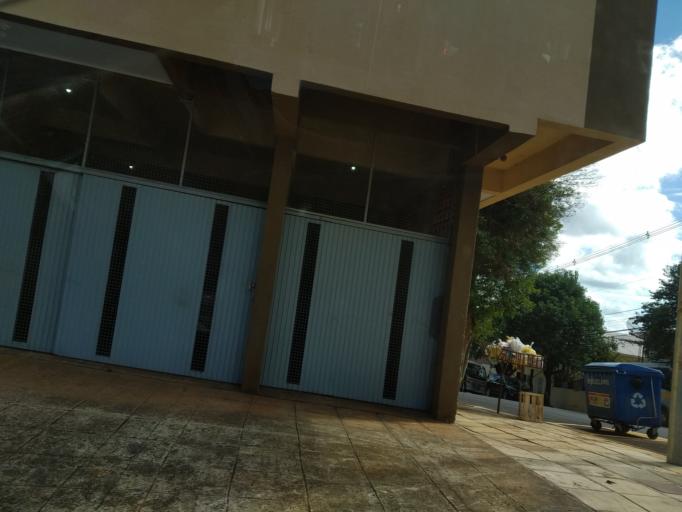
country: BR
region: Parana
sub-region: Pato Branco
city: Pato Branco
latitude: -26.2295
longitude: -52.6674
